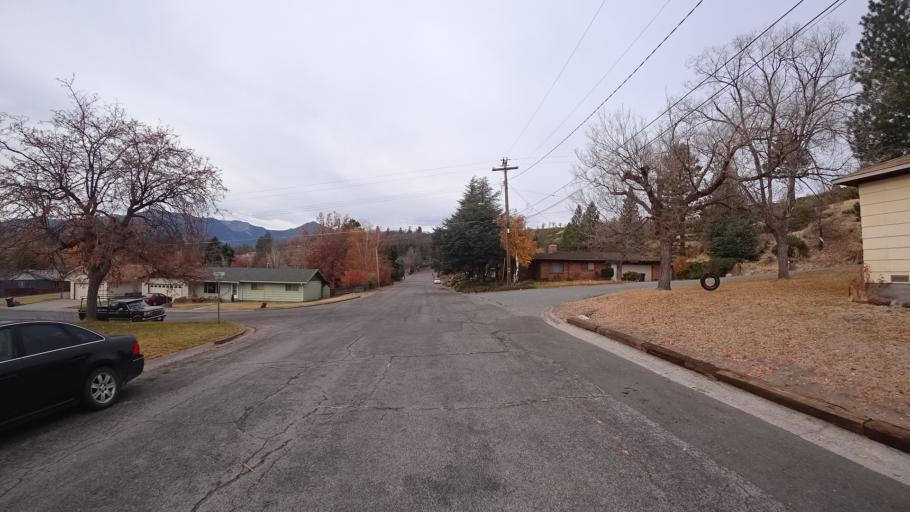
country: US
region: California
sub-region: Siskiyou County
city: Weed
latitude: 41.4176
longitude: -122.3888
